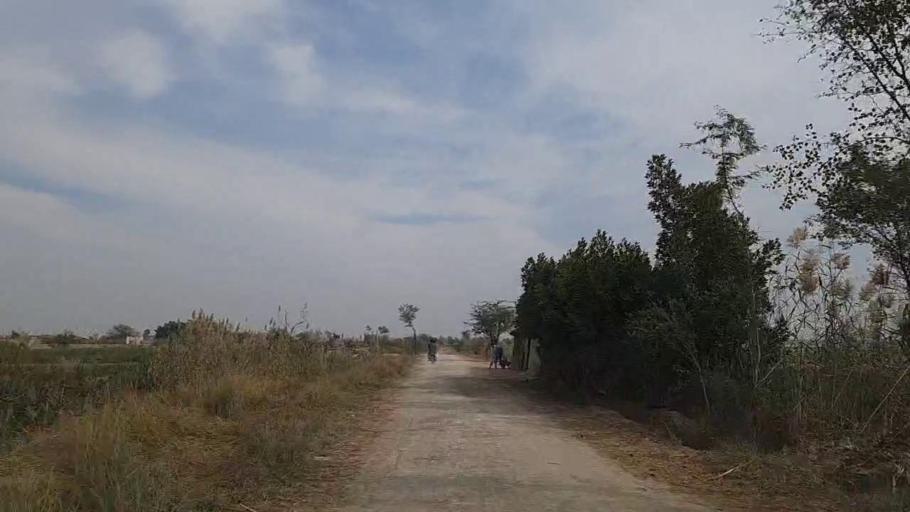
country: PK
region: Sindh
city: Daur
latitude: 26.4992
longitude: 68.3944
